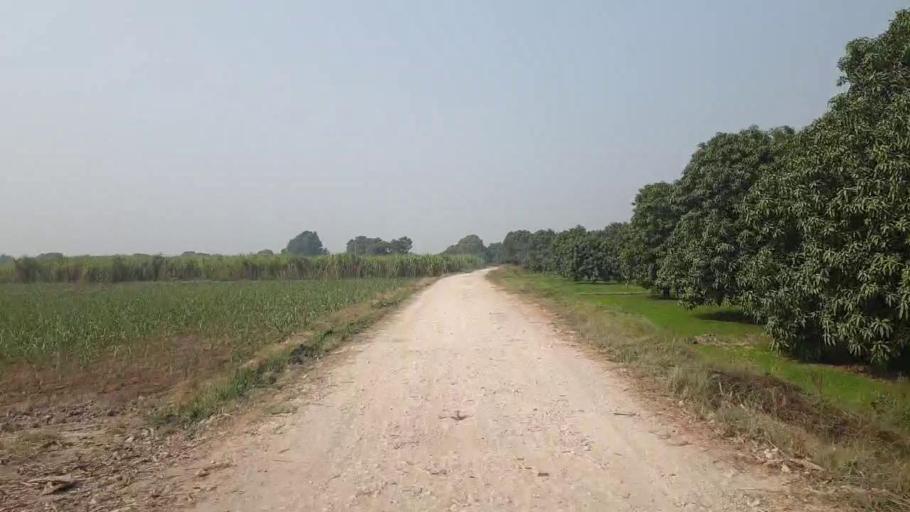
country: PK
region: Sindh
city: Tando Muhammad Khan
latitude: 25.2667
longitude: 68.5883
